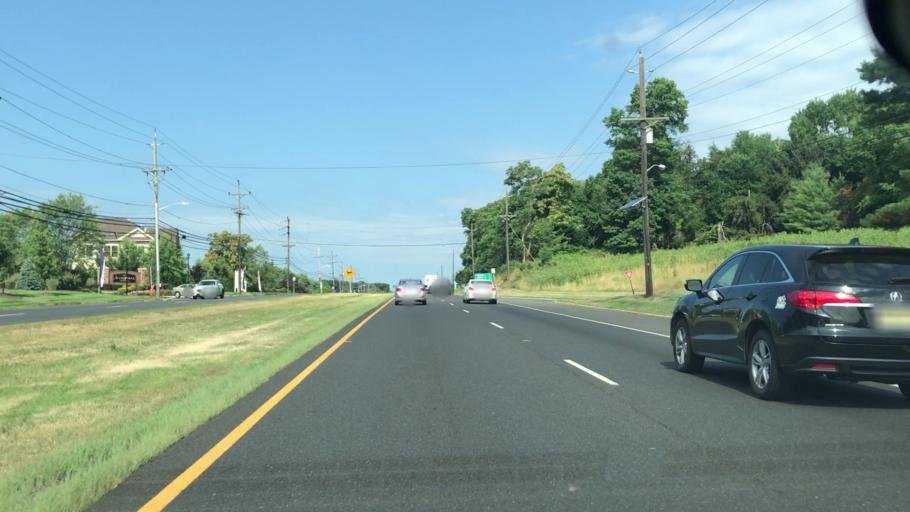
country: US
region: New Jersey
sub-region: Somerset County
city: Raritan
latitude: 40.5744
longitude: -74.6437
